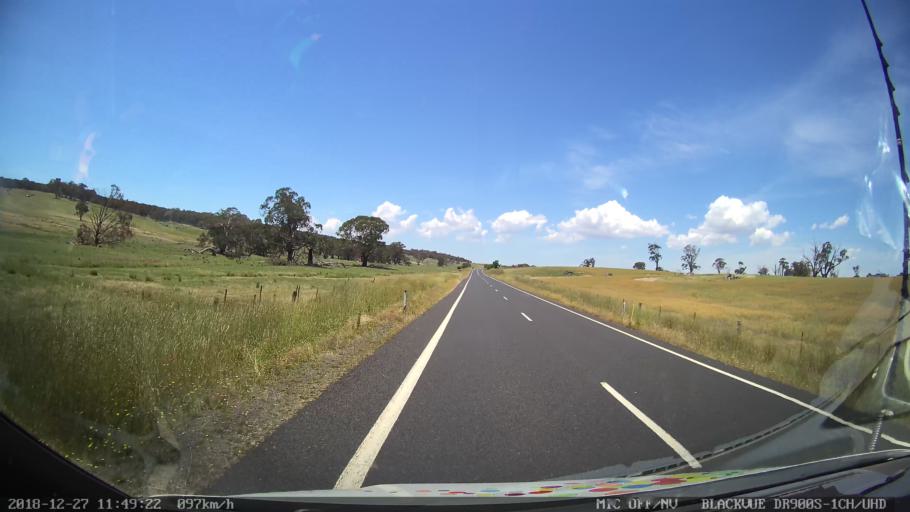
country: AU
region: New South Wales
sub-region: Bathurst Regional
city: Perthville
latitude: -33.6184
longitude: 149.4352
